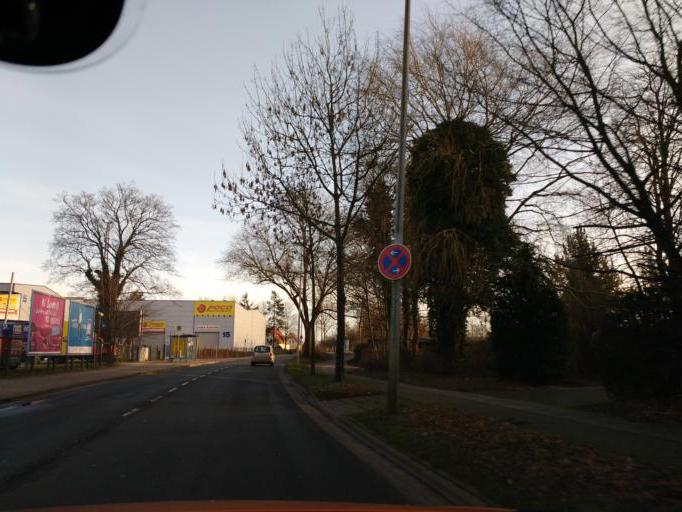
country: DE
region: Lower Saxony
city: Oldenburg
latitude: 53.1383
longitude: 8.2383
